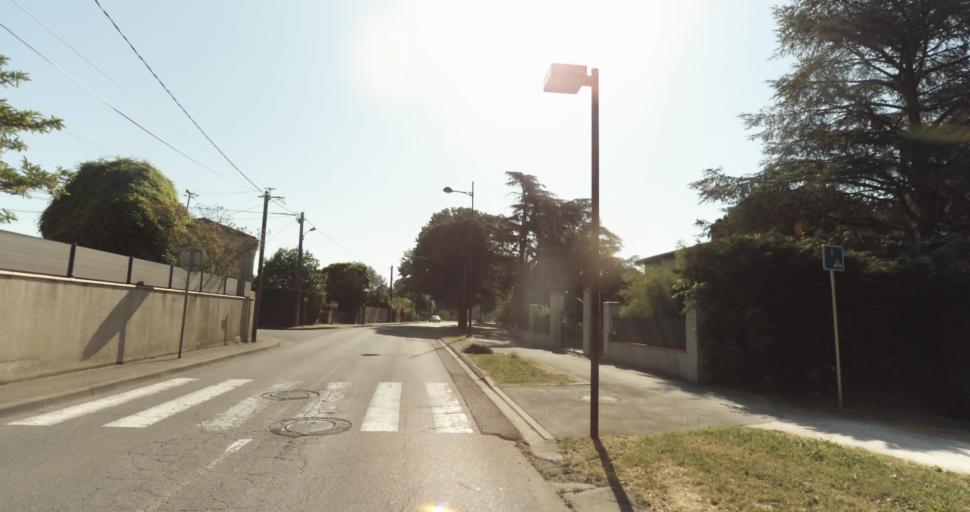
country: FR
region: Midi-Pyrenees
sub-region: Departement de la Haute-Garonne
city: Plaisance-du-Touch
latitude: 43.5662
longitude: 1.3023
